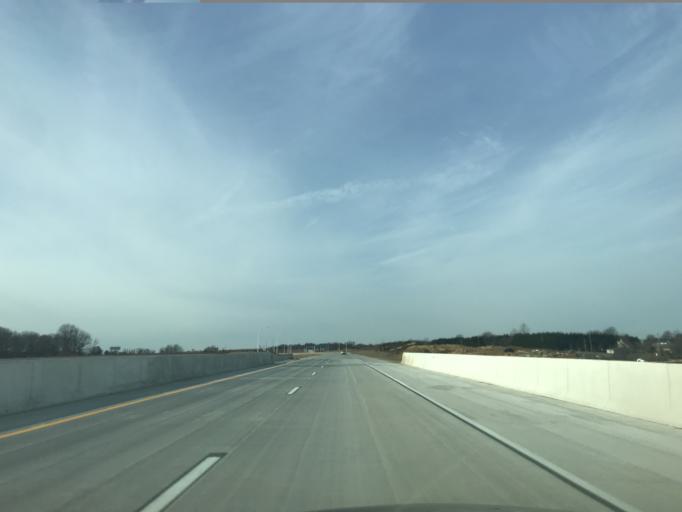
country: US
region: Delaware
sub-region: New Castle County
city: Middletown
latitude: 39.5246
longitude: -75.6660
